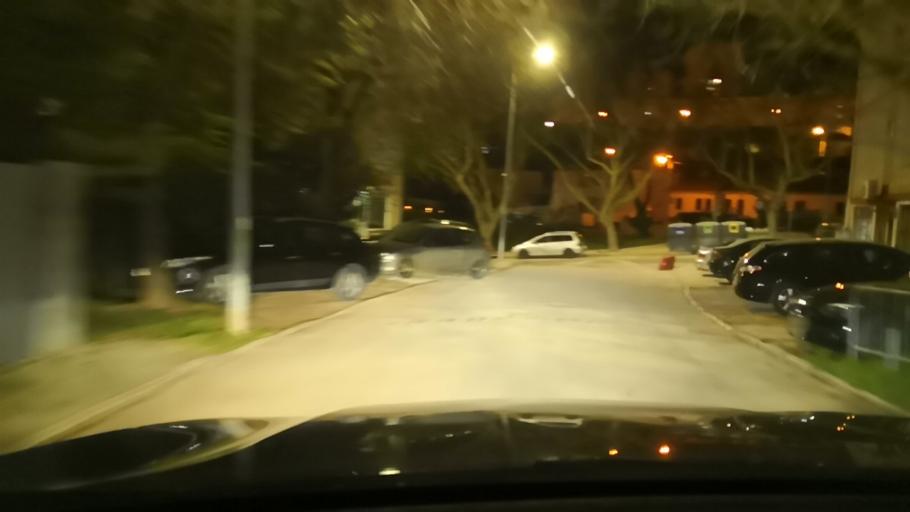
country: PT
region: Setubal
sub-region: Setubal
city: Setubal
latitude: 38.5276
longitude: -8.9021
